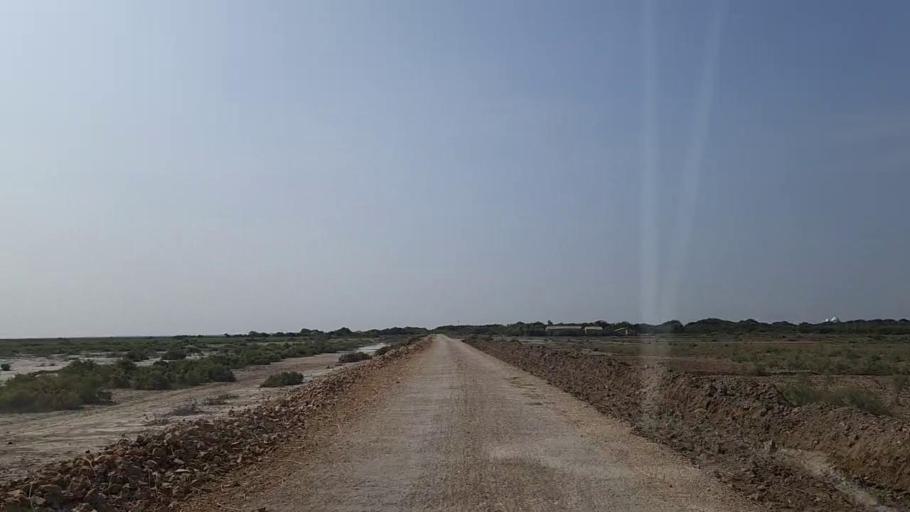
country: PK
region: Sindh
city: Chuhar Jamali
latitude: 24.2006
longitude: 67.8239
